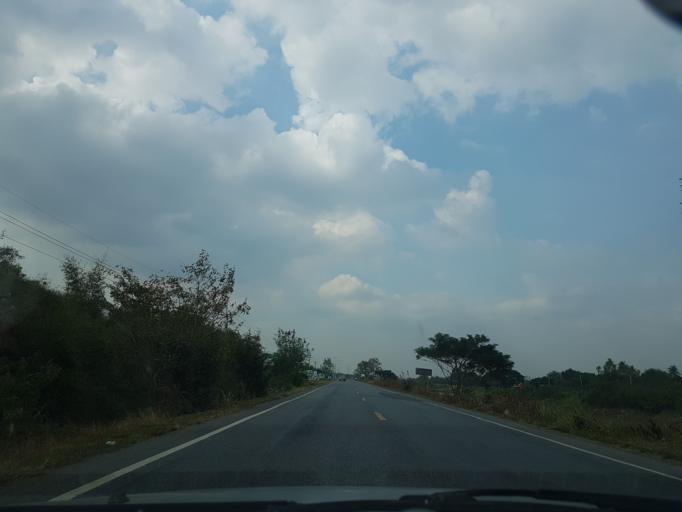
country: TH
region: Phra Nakhon Si Ayutthaya
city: Phachi
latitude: 14.4759
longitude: 100.7446
